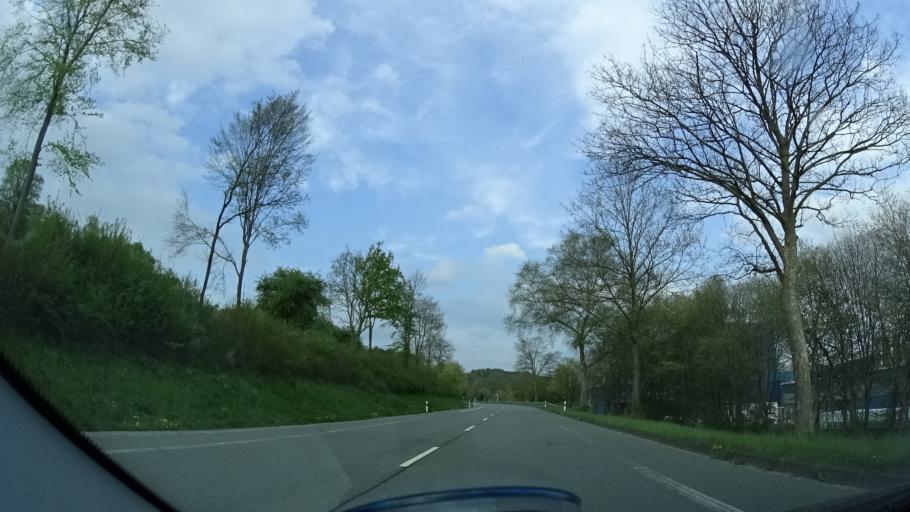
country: DE
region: North Rhine-Westphalia
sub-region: Regierungsbezirk Arnsberg
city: Ruthen
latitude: 51.4849
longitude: 8.4359
